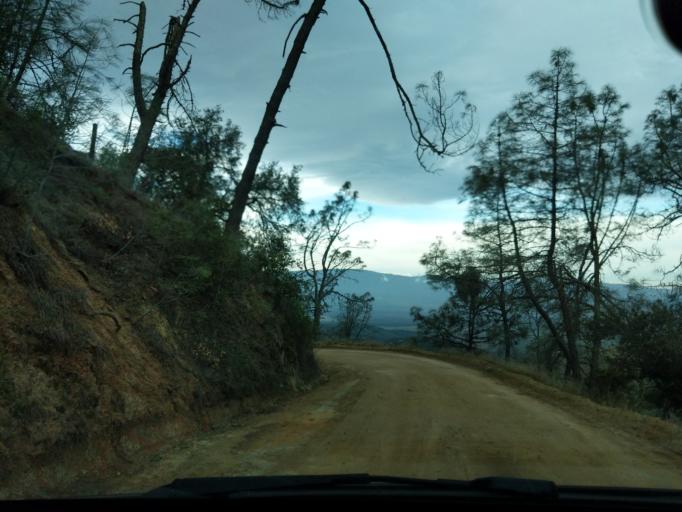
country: US
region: California
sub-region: Monterey County
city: Soledad
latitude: 36.5350
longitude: -121.3017
